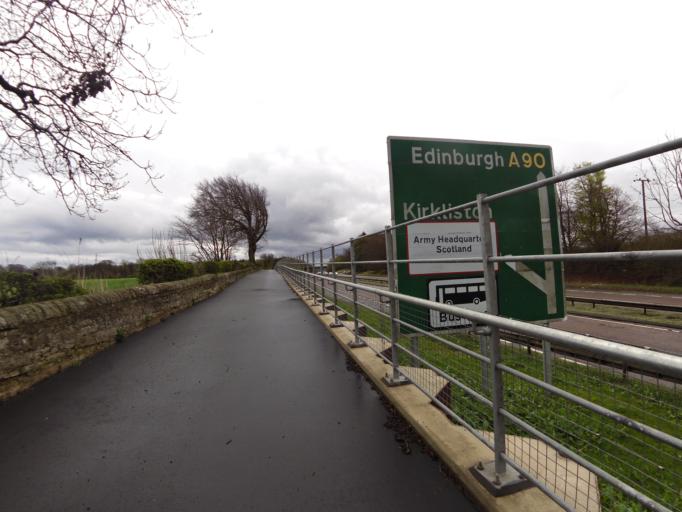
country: GB
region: Scotland
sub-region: Edinburgh
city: Queensferry
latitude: 55.9738
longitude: -3.3335
